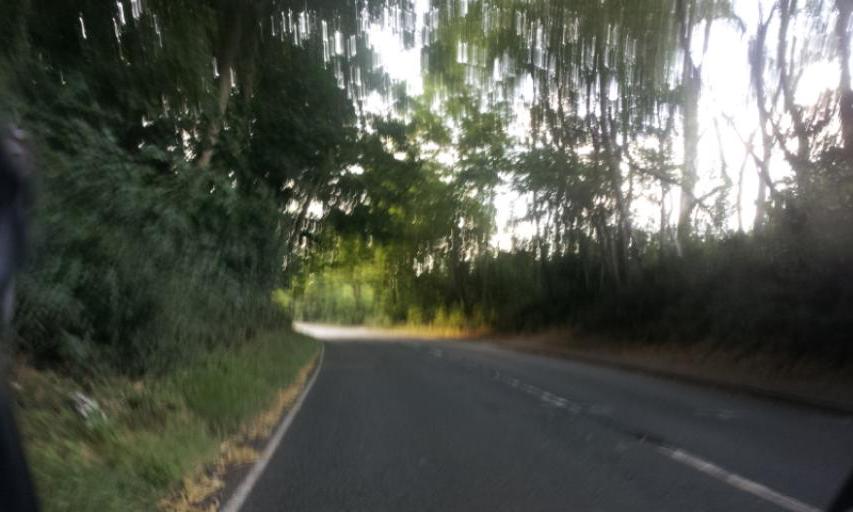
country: GB
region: England
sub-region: Kent
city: Boxley
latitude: 51.2915
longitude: 0.5246
